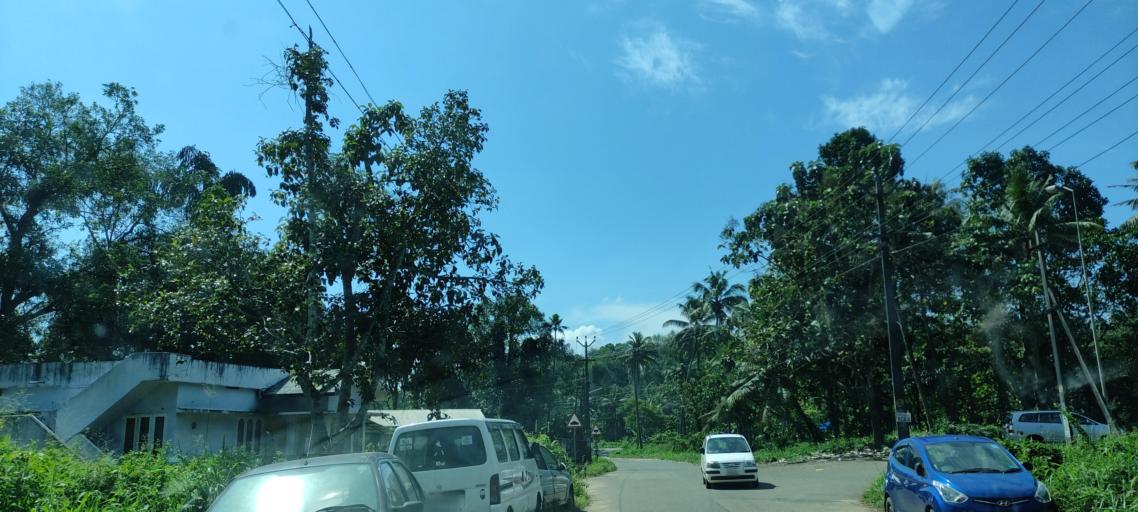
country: IN
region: Kerala
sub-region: Pattanamtitta
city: Adur
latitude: 9.1559
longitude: 76.7272
